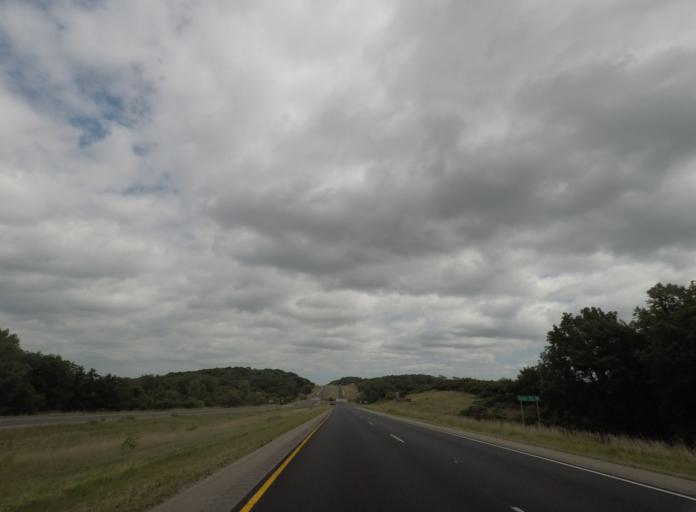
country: US
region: Iowa
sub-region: Linn County
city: Ely
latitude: 41.9254
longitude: -91.5826
